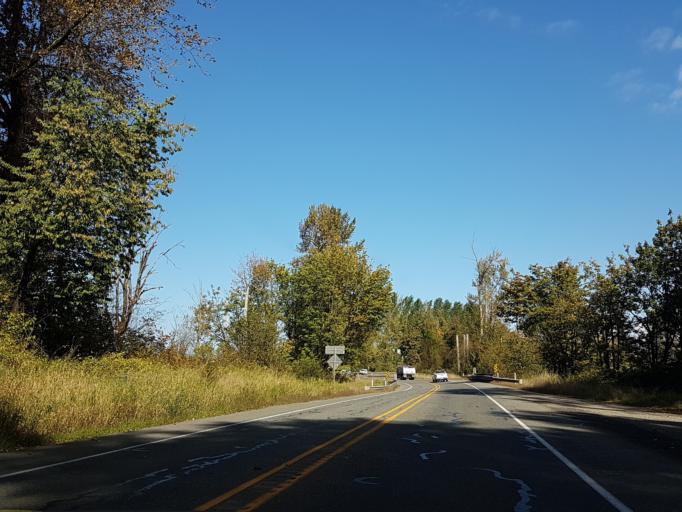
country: US
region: Washington
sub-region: Snohomish County
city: Monroe
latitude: 47.8135
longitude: -121.9820
